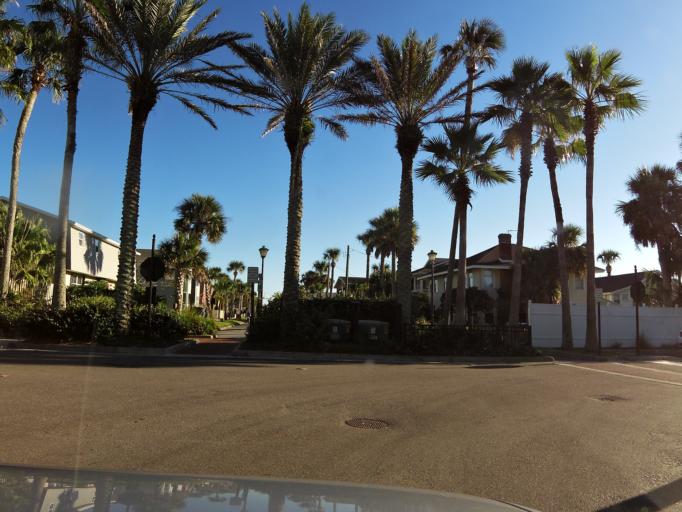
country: US
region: Florida
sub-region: Duval County
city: Neptune Beach
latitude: 30.3229
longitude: -81.3959
